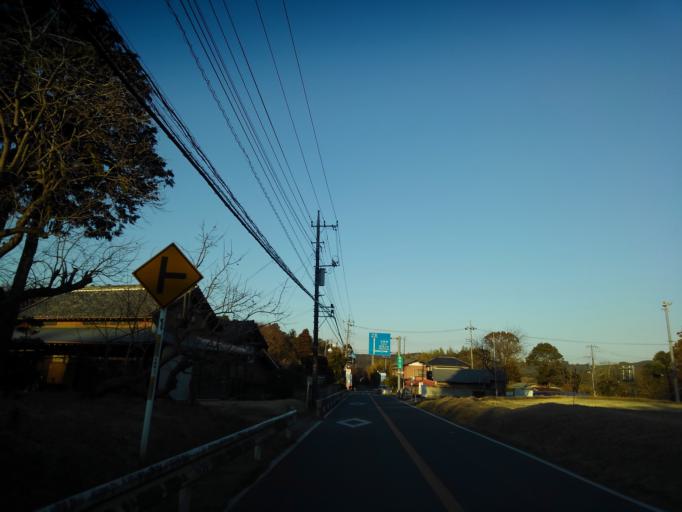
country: JP
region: Chiba
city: Kimitsu
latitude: 35.2938
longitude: 139.9784
